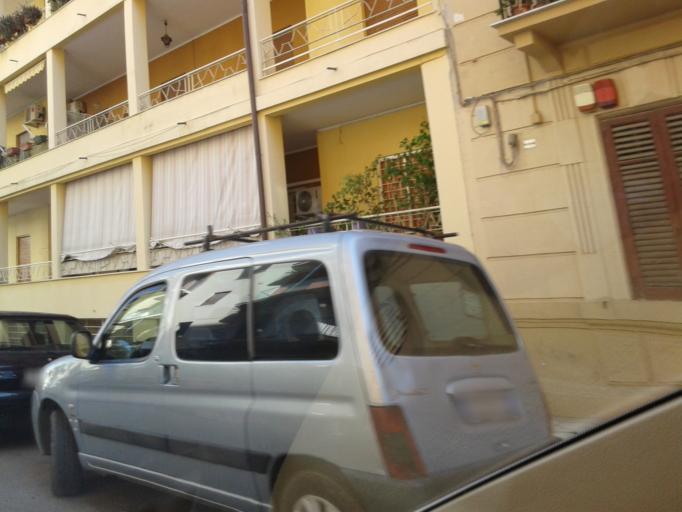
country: IT
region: Sicily
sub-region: Palermo
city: Palermo
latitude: 38.1358
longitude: 13.3473
